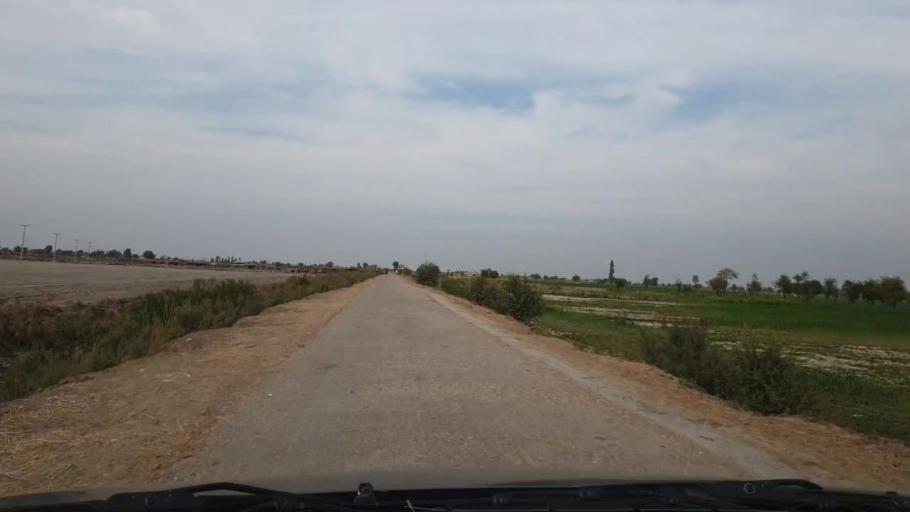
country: PK
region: Sindh
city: Khadro
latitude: 26.1571
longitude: 68.7304
